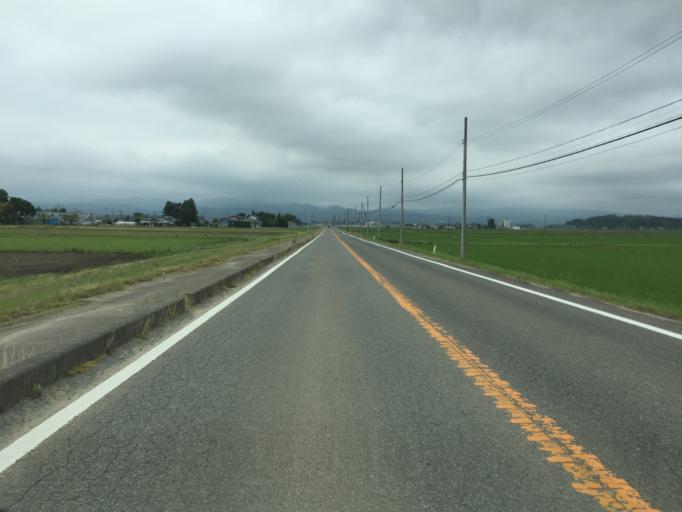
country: JP
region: Fukushima
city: Namie
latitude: 37.7064
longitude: 140.9899
